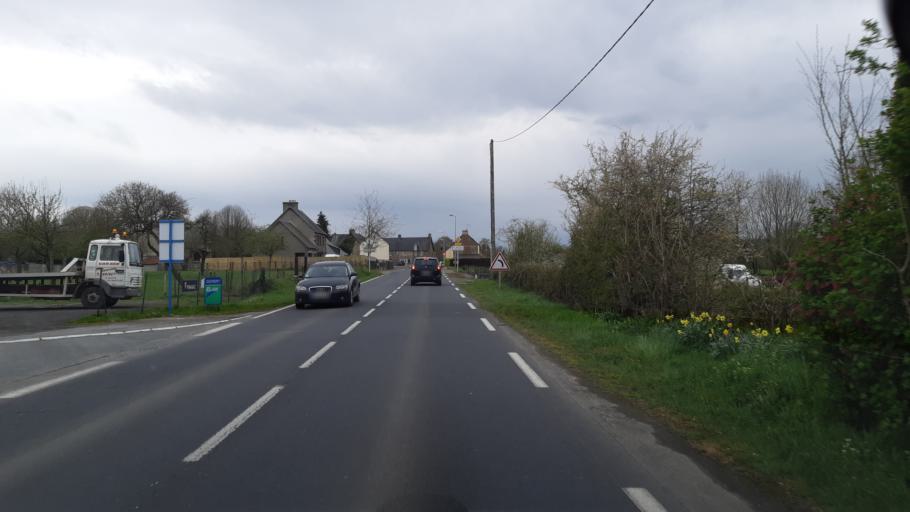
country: FR
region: Lower Normandy
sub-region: Departement de la Manche
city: Agneaux
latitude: 49.0292
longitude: -1.1418
